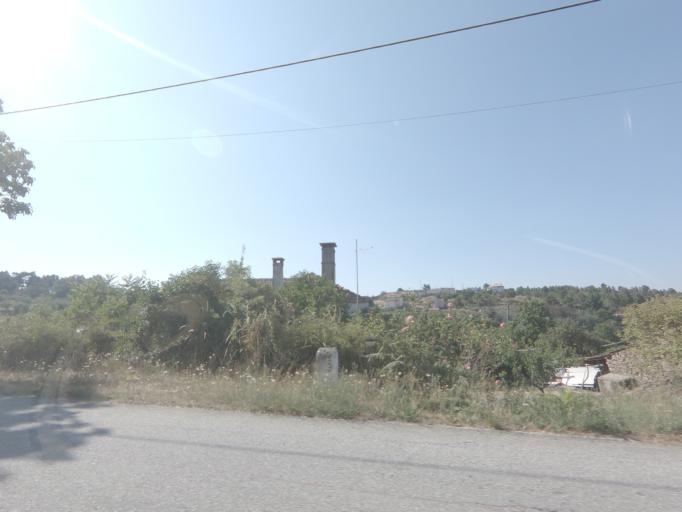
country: PT
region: Viseu
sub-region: Moimenta da Beira
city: Moimenta da Beira
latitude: 40.9806
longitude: -7.6011
